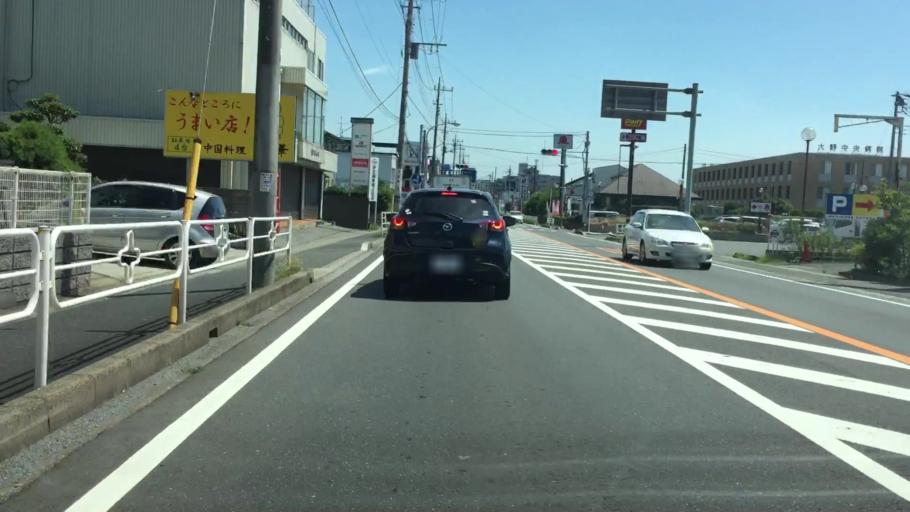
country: JP
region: Chiba
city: Funabashi
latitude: 35.7415
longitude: 139.9480
